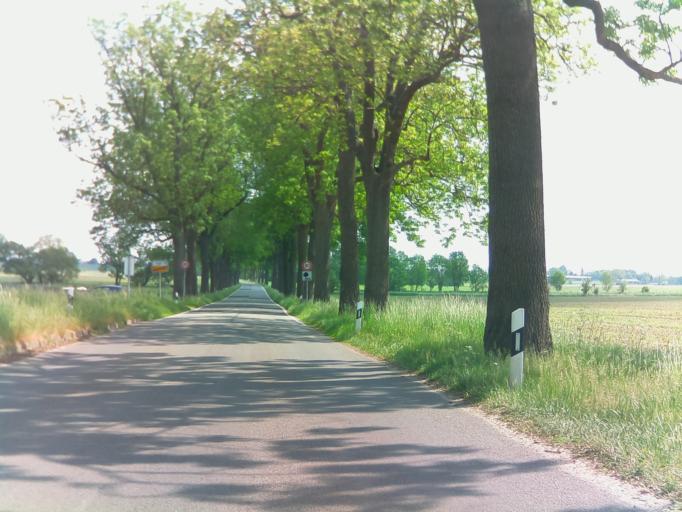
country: DE
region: Brandenburg
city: Kotzen
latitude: 52.6140
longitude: 12.5718
